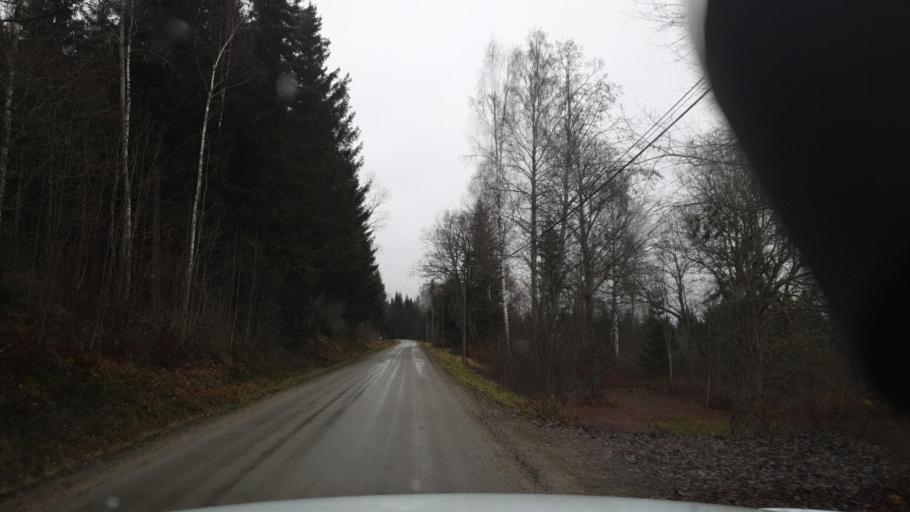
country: SE
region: Vaermland
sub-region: Eda Kommun
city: Amotfors
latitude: 59.7437
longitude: 12.2763
